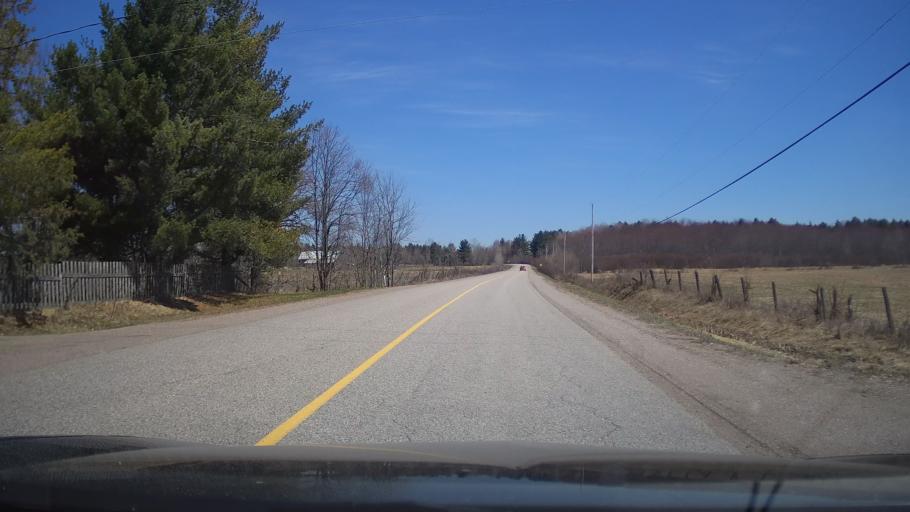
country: CA
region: Ontario
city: Arnprior
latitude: 45.5387
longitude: -76.3682
